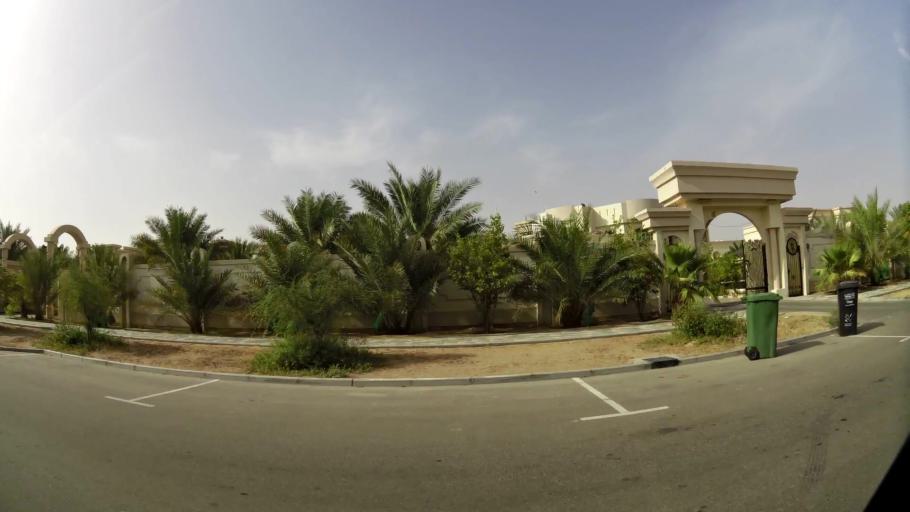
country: AE
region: Abu Dhabi
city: Al Ain
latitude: 24.1511
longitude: 55.7214
